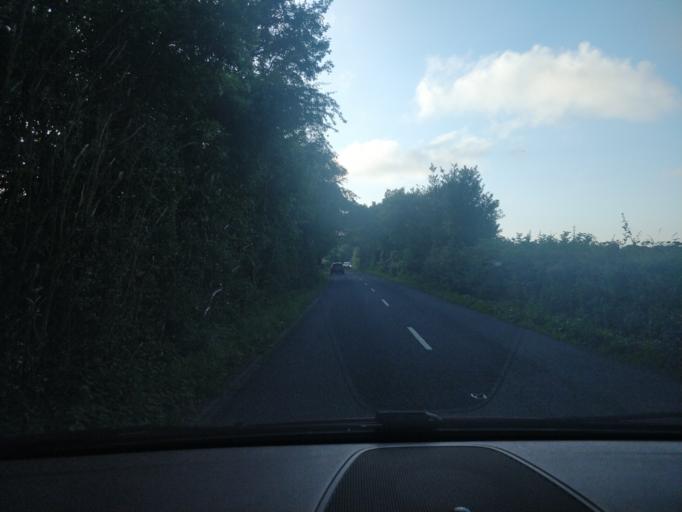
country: GB
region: England
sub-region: Lancashire
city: Skelmersdale
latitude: 53.5583
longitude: -2.7482
